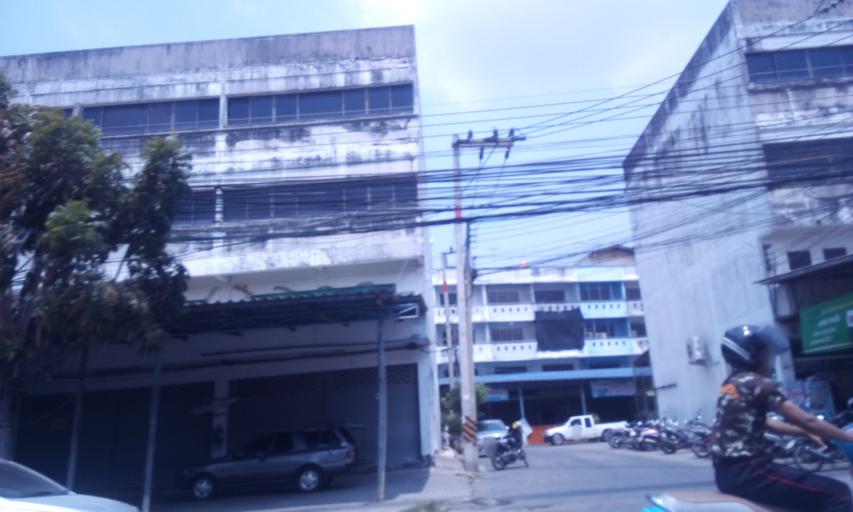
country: TH
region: Chachoengsao
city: Chachoengsao
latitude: 13.6663
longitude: 101.0916
